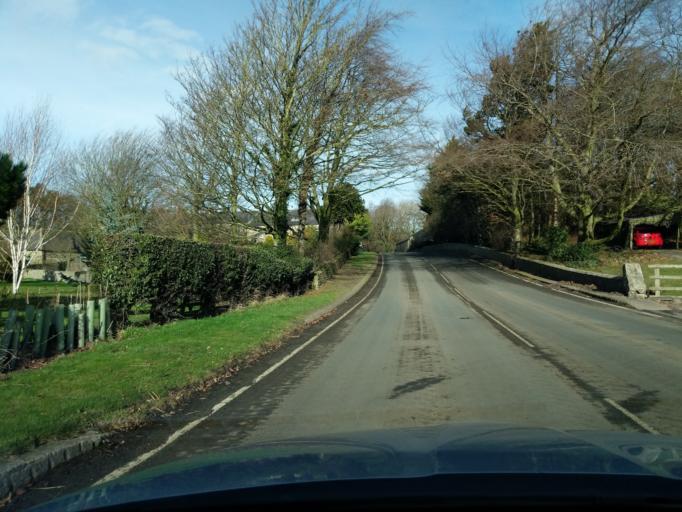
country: GB
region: England
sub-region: North Yorkshire
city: Catterick Garrison
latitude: 54.3452
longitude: -1.6914
